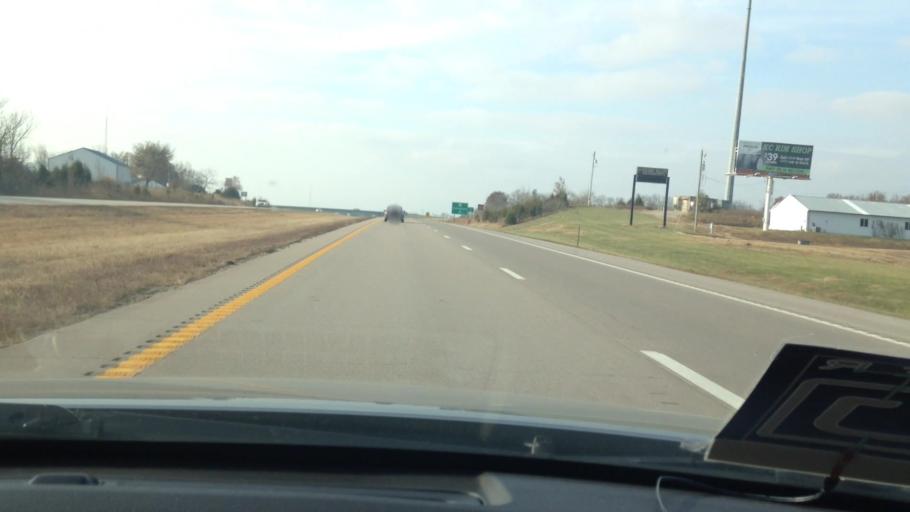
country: US
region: Missouri
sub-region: Cass County
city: Garden City
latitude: 38.4975
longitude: -94.0645
